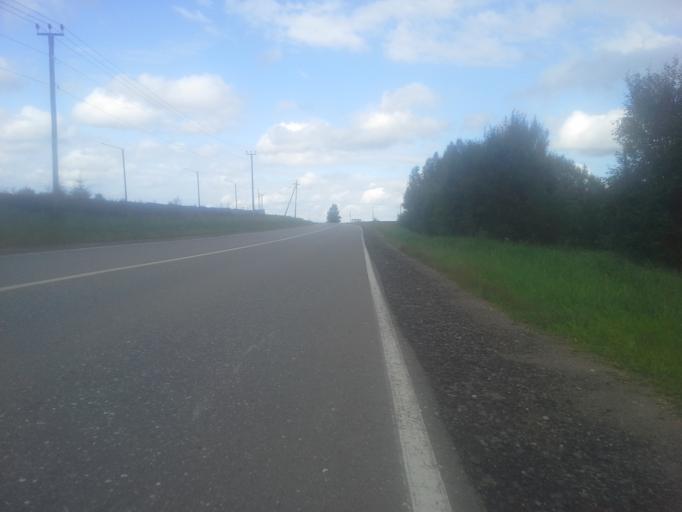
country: RU
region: Moskovskaya
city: Karinskoye
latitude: 55.6726
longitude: 36.6558
